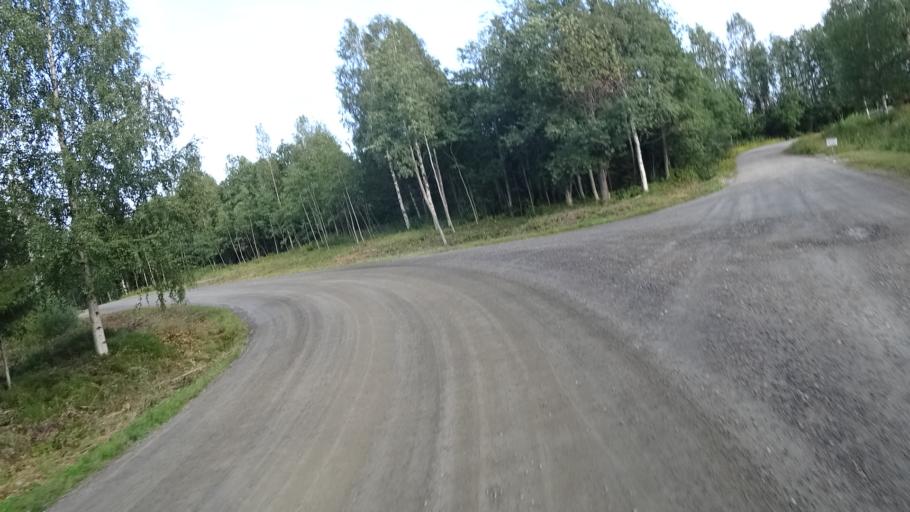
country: FI
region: North Karelia
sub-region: Joensuu
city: Ilomantsi
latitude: 62.6699
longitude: 30.9483
